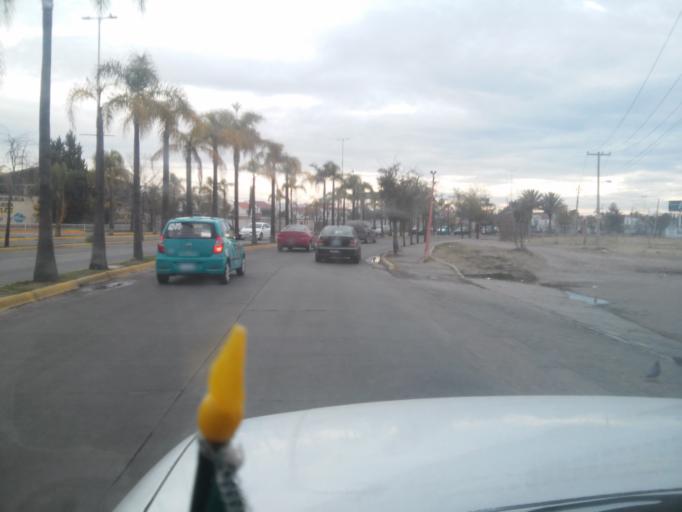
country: MX
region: Durango
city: Victoria de Durango
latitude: 24.0029
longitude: -104.6506
